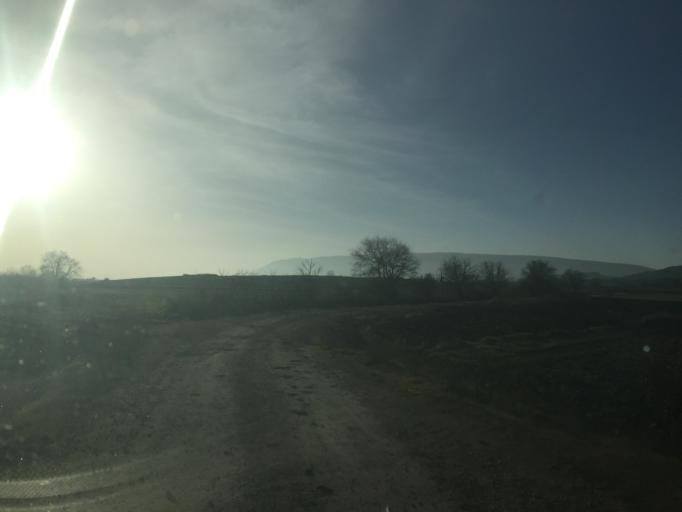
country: ES
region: Castille and Leon
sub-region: Provincia de Burgos
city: Medina de Pomar
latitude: 42.9385
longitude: -3.5949
